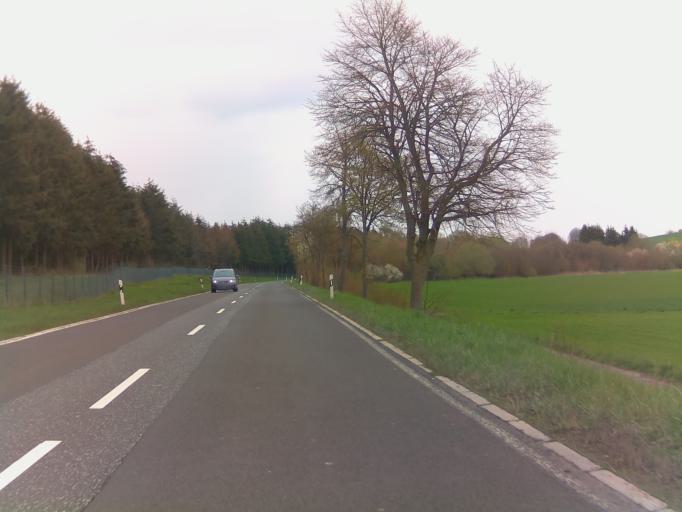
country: DE
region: Rheinland-Pfalz
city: Auen
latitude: 49.8527
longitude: 7.5857
